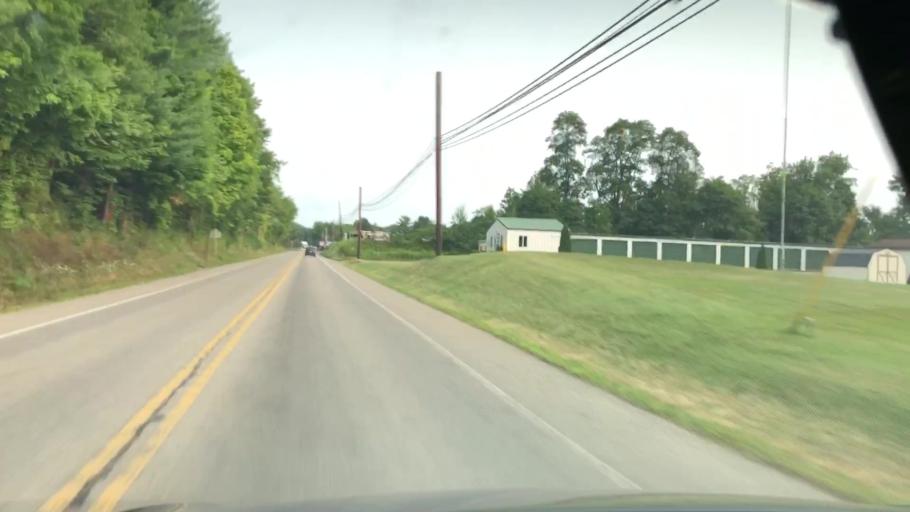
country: US
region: Pennsylvania
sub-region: Crawford County
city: Titusville
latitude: 41.6531
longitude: -79.7233
